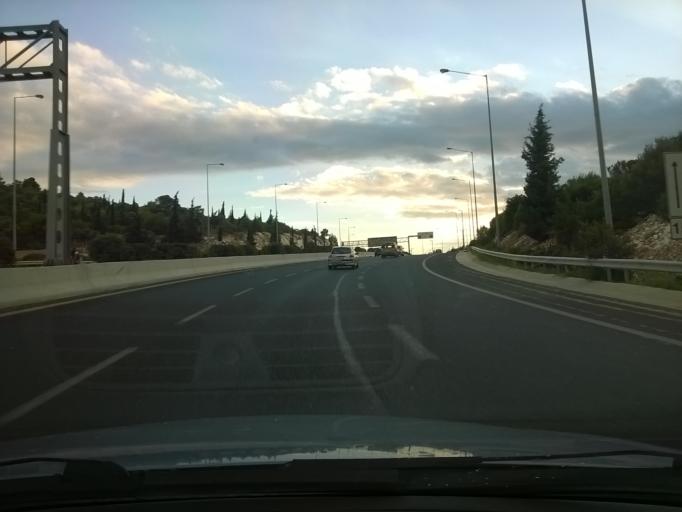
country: GR
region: Attica
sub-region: Nomos Attikis
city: Zografos
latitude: 37.9718
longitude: 23.7933
